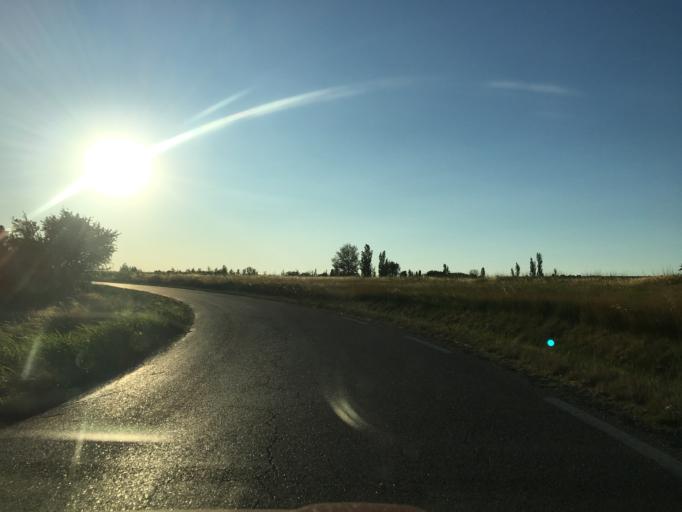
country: FR
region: Provence-Alpes-Cote d'Azur
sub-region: Departement des Bouches-du-Rhone
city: Eyragues
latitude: 43.8415
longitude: 4.8822
